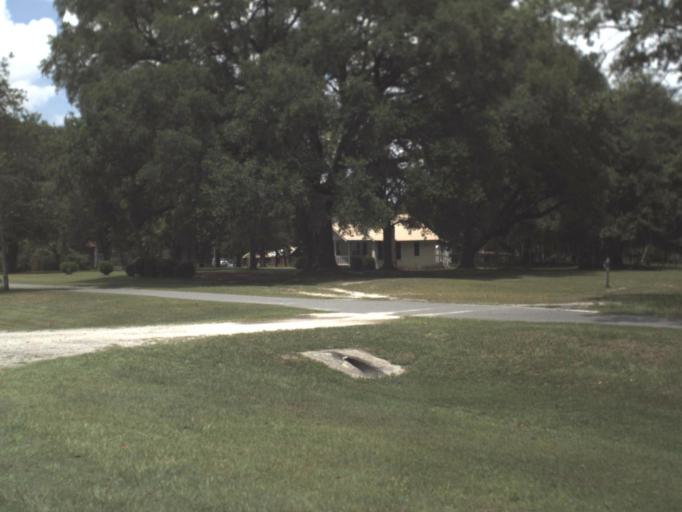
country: US
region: Florida
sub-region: Madison County
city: Madison
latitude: 30.5489
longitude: -83.3675
